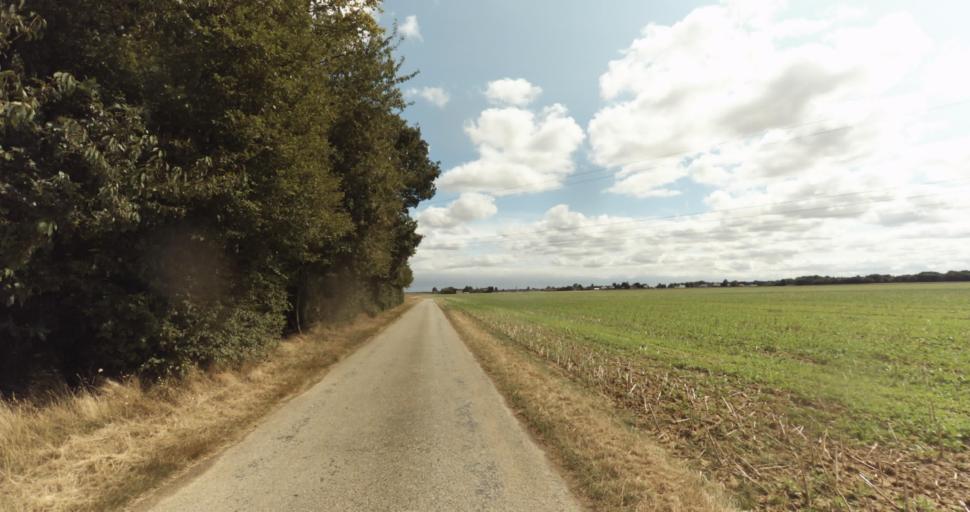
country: FR
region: Haute-Normandie
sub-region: Departement de l'Eure
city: Damville
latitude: 48.8620
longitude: 1.1546
